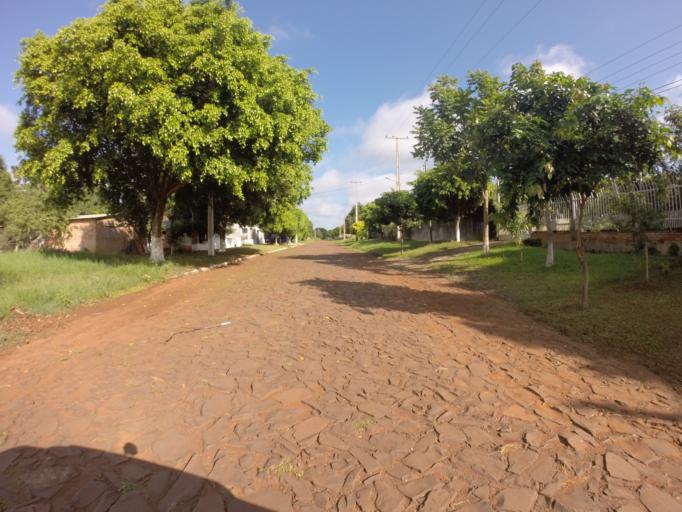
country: PY
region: Alto Parana
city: Ciudad del Este
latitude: -25.4093
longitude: -54.6460
